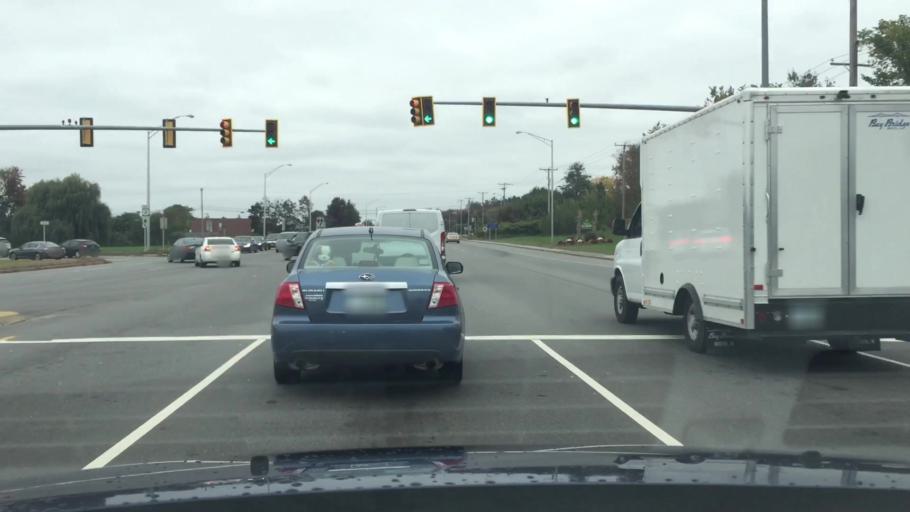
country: US
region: New Hampshire
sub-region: Hillsborough County
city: Hudson
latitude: 42.7287
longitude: -71.4250
